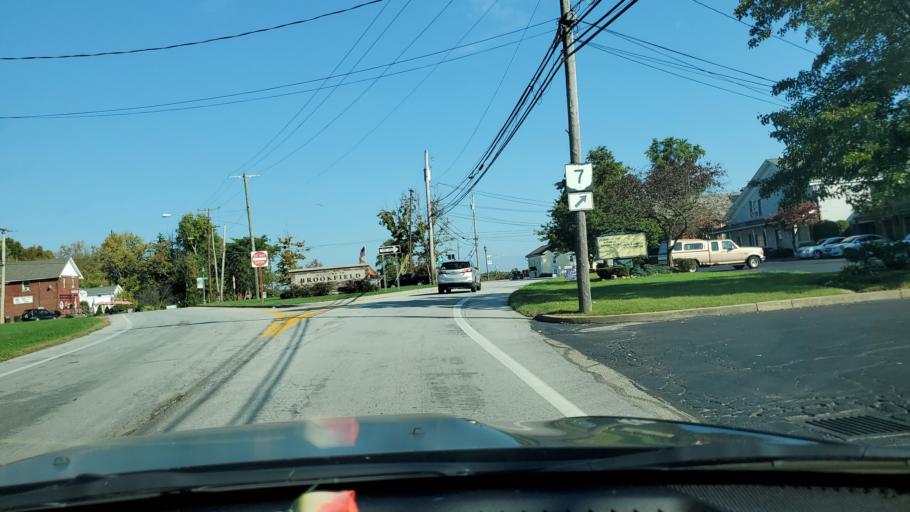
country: US
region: Ohio
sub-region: Trumbull County
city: Brookfield Center
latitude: 41.2319
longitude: -80.5680
